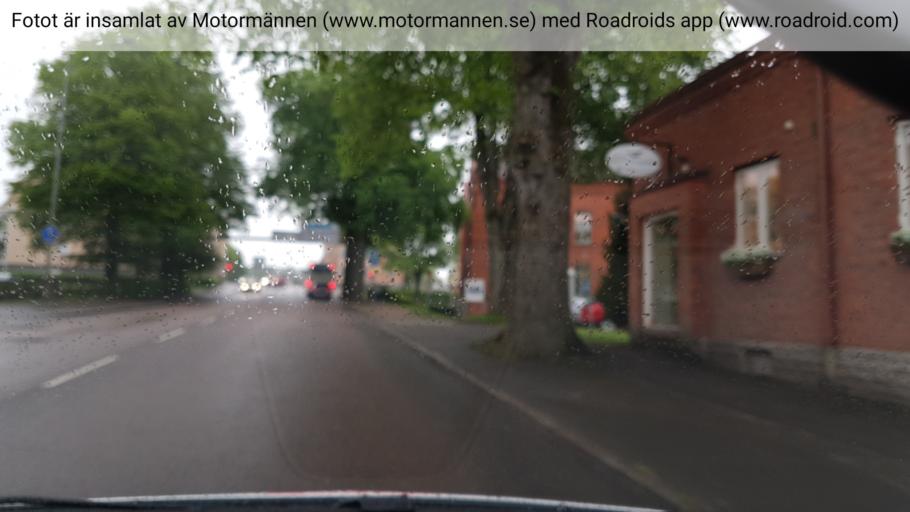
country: SE
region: Vaestra Goetaland
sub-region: Falkopings Kommun
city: Falkoeping
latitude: 58.1650
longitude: 13.5541
